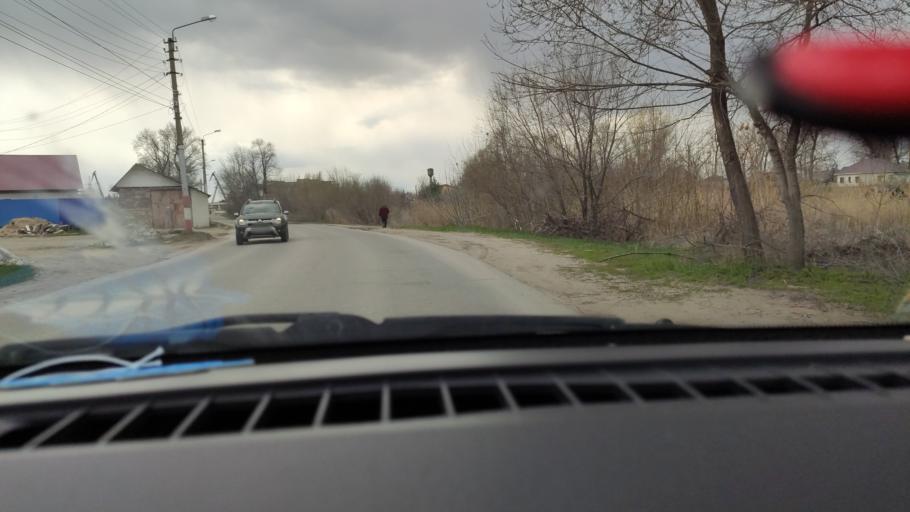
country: RU
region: Saratov
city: Engel's
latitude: 51.4908
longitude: 46.0517
